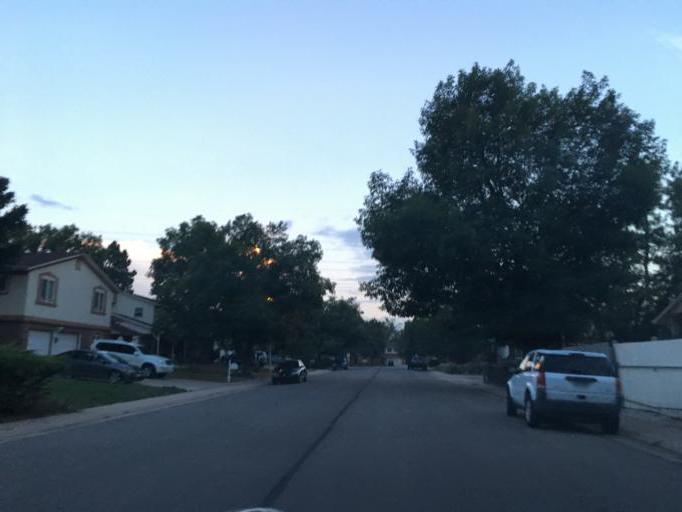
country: US
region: Colorado
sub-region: Adams County
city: Aurora
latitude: 39.6833
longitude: -104.8507
